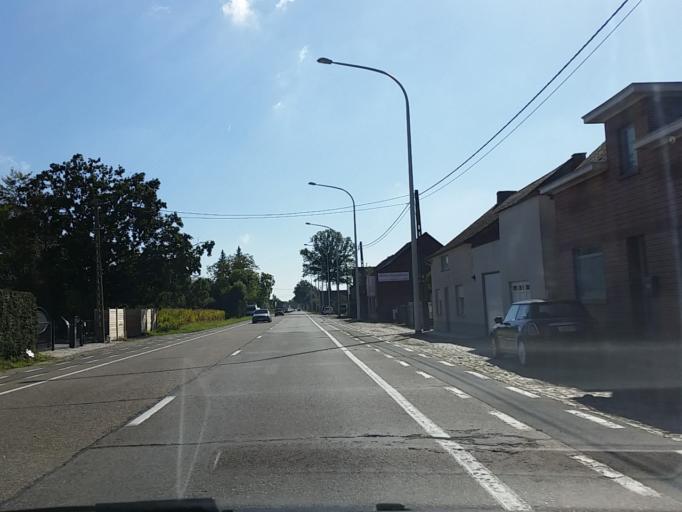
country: BE
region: Flanders
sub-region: Provincie Vlaams-Brabant
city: Herent
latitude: 50.9225
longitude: 4.6447
